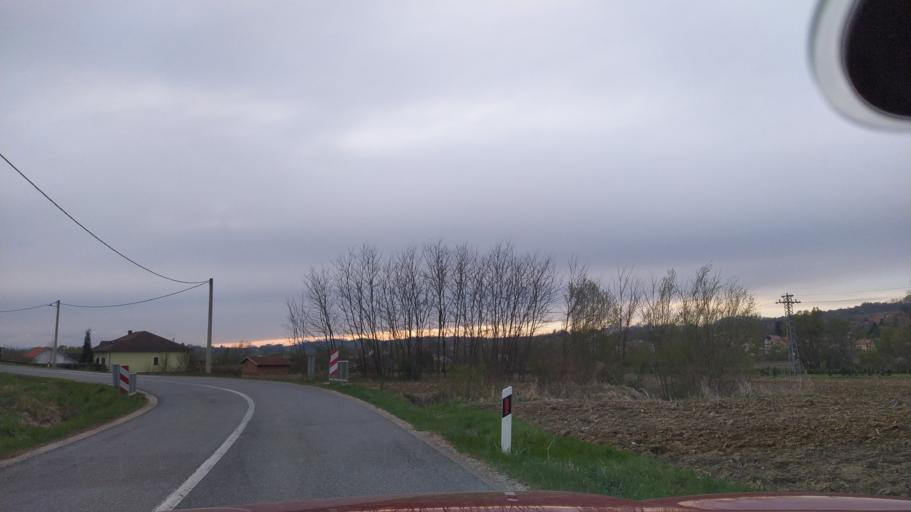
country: HR
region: Varazdinska
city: Jalzabet
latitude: 46.2150
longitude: 16.5094
